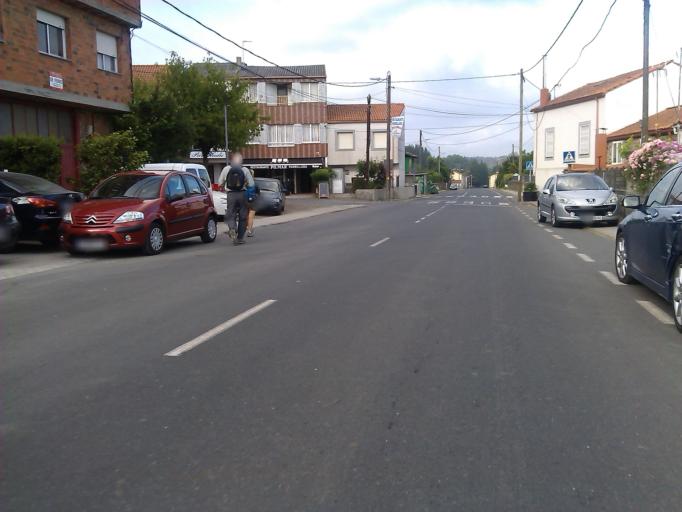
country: ES
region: Galicia
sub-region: Provincia da Coruna
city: Melide
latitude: 42.9115
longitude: -8.0240
